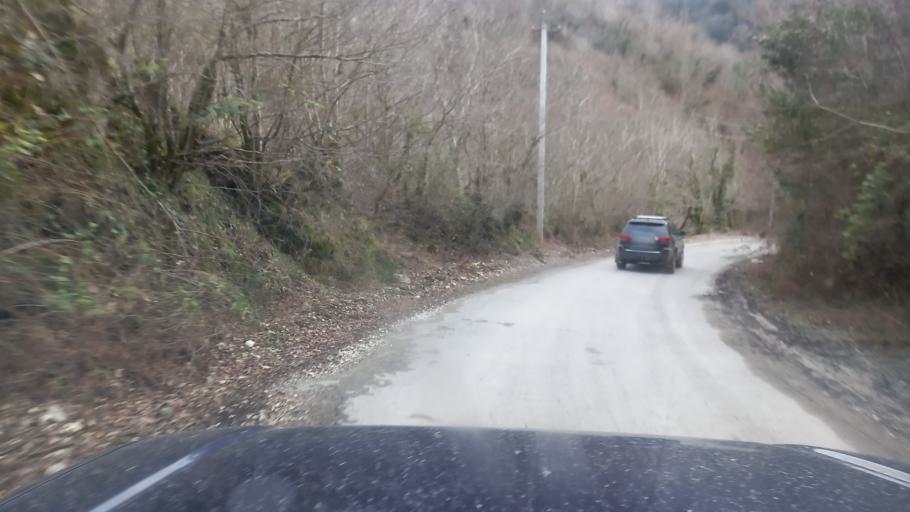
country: GE
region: Abkhazia
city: Gulrip'shi
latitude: 43.0159
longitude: 41.2290
